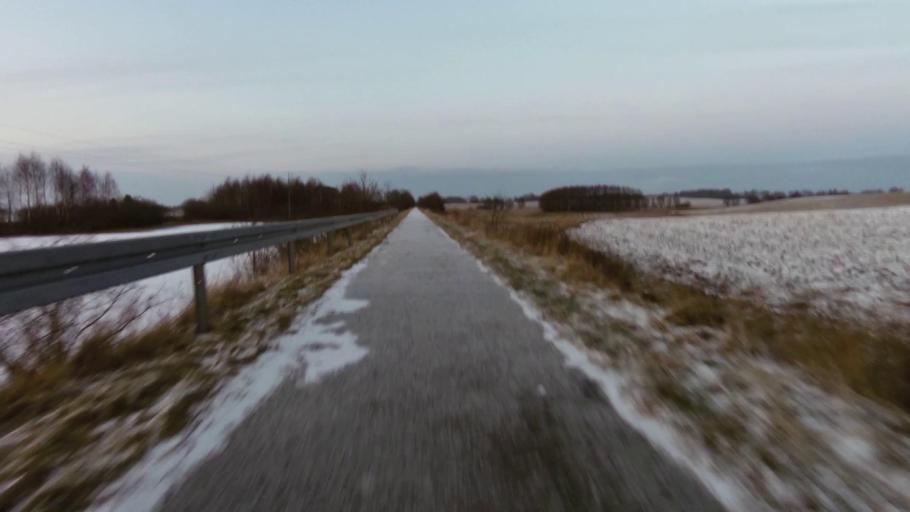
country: PL
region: West Pomeranian Voivodeship
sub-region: Powiat swidwinski
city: Polczyn-Zdroj
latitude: 53.7179
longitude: 16.0400
